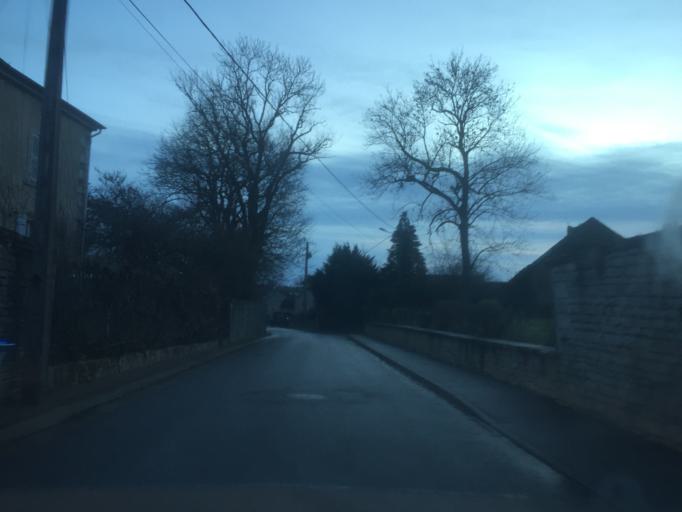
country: FR
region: Franche-Comte
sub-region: Departement du Jura
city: Orchamps
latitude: 47.1453
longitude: 5.6821
